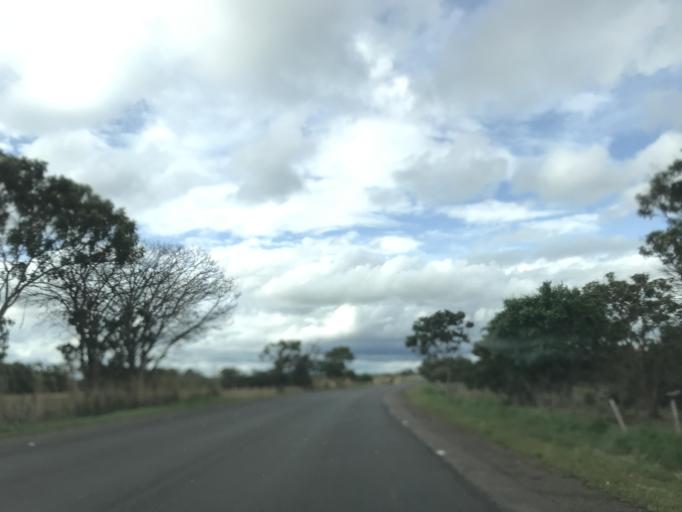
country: BR
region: Goias
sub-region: Bela Vista De Goias
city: Bela Vista de Goias
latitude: -16.9974
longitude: -48.6703
